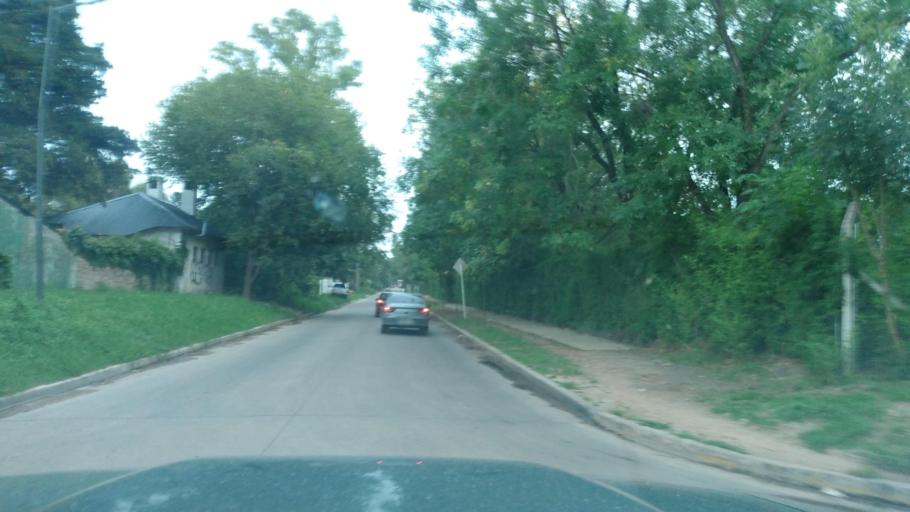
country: AR
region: Buenos Aires
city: Hurlingham
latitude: -34.5596
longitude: -58.7248
